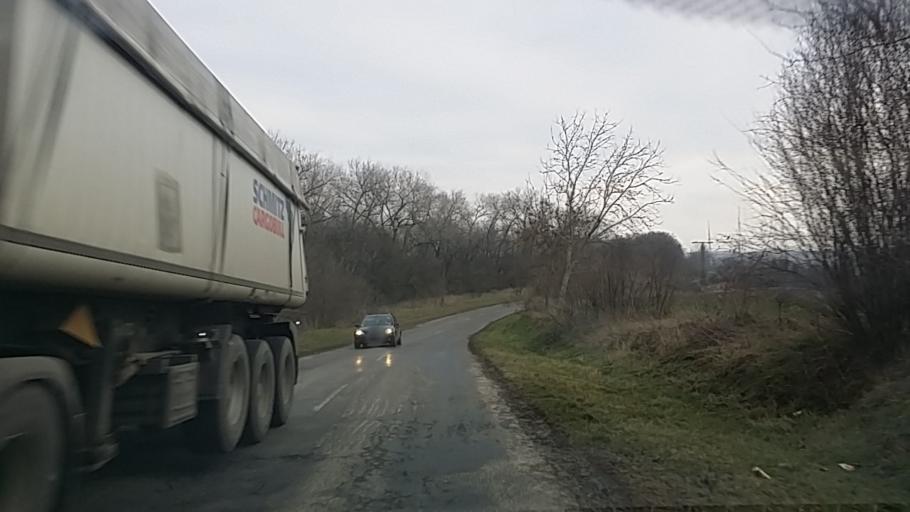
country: HU
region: Baranya
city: Lanycsok
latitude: 46.1033
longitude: 18.5427
